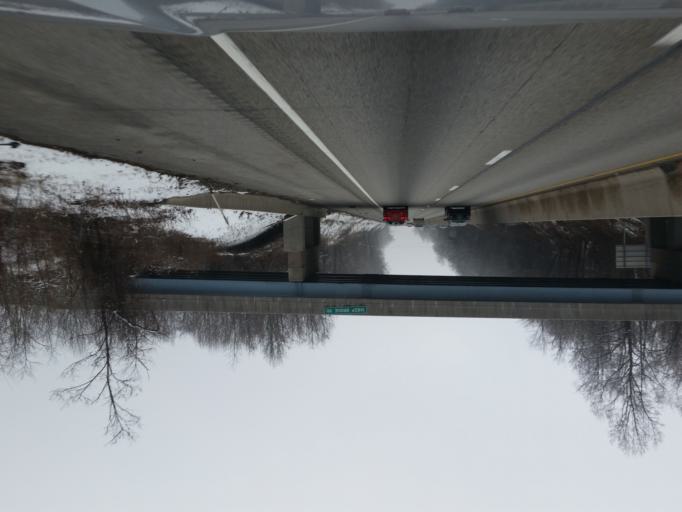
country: US
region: Pennsylvania
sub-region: York County
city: Valley Green
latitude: 40.1200
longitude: -76.7888
